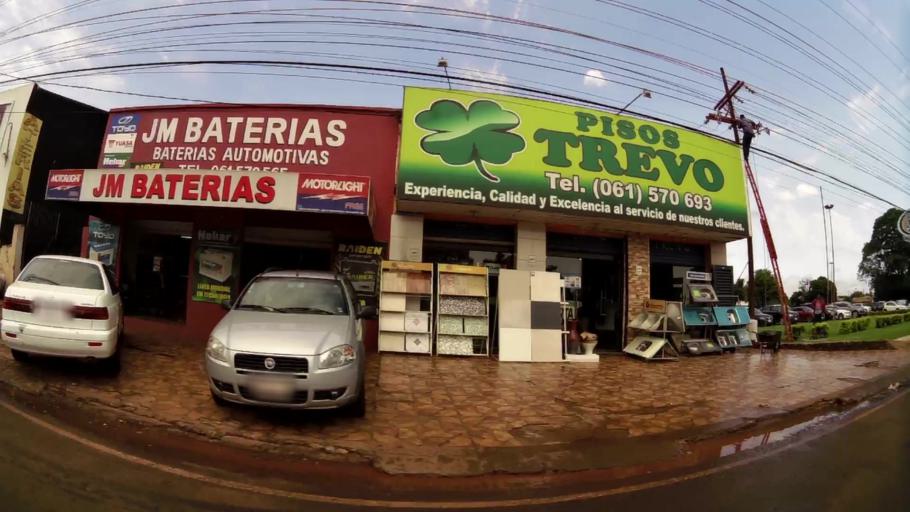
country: PY
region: Alto Parana
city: Ciudad del Este
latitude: -25.4995
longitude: -54.6622
